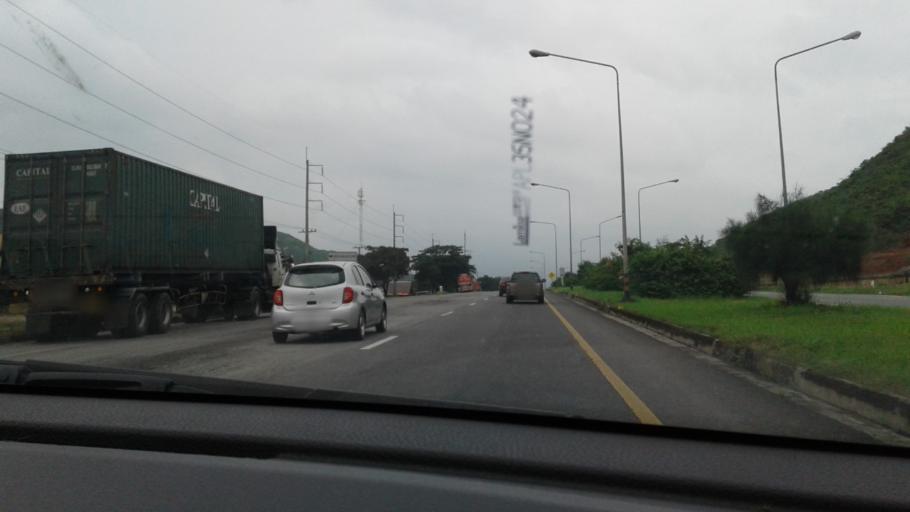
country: TH
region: Prachuap Khiri Khan
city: Prachuap Khiri Khan
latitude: 11.9060
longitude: 99.7964
